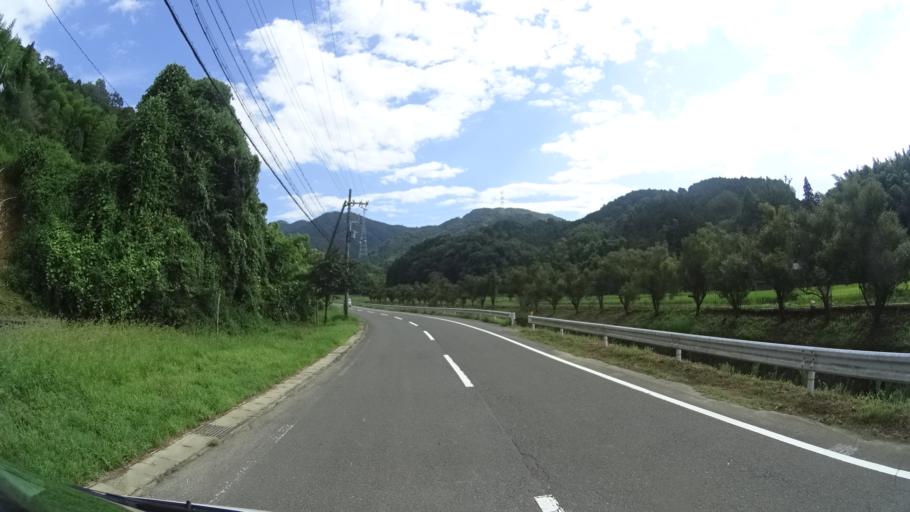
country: JP
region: Kyoto
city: Fukuchiyama
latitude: 35.3670
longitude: 135.1312
